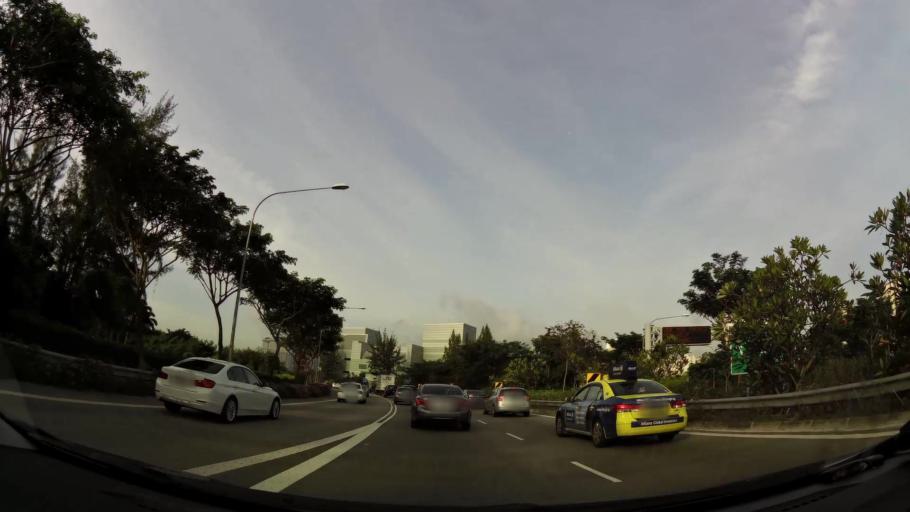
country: SG
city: Singapore
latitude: 1.2951
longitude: 103.8775
